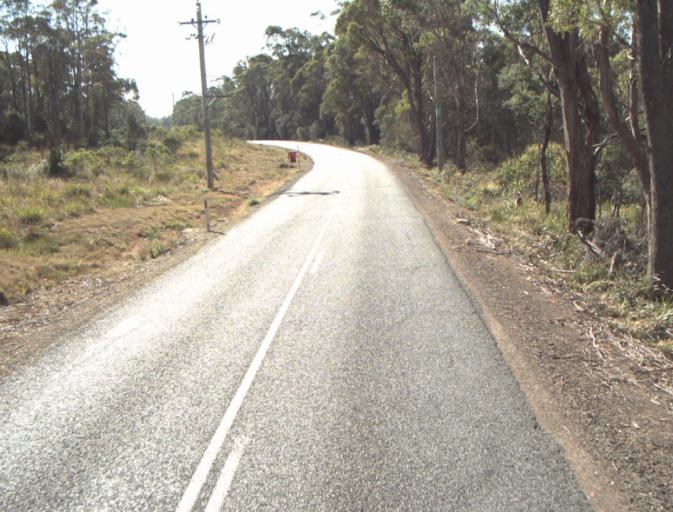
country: AU
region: Tasmania
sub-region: Launceston
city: Mayfield
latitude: -41.3298
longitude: 147.1404
